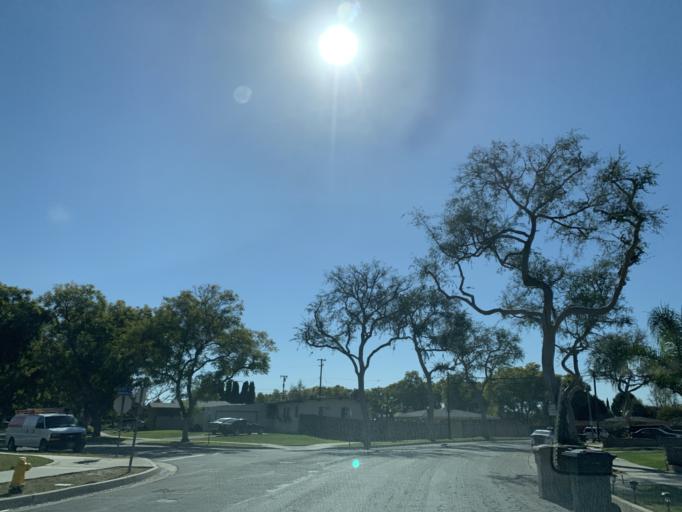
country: US
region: California
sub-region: Orange County
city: Placentia
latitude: 33.8804
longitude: -117.8964
